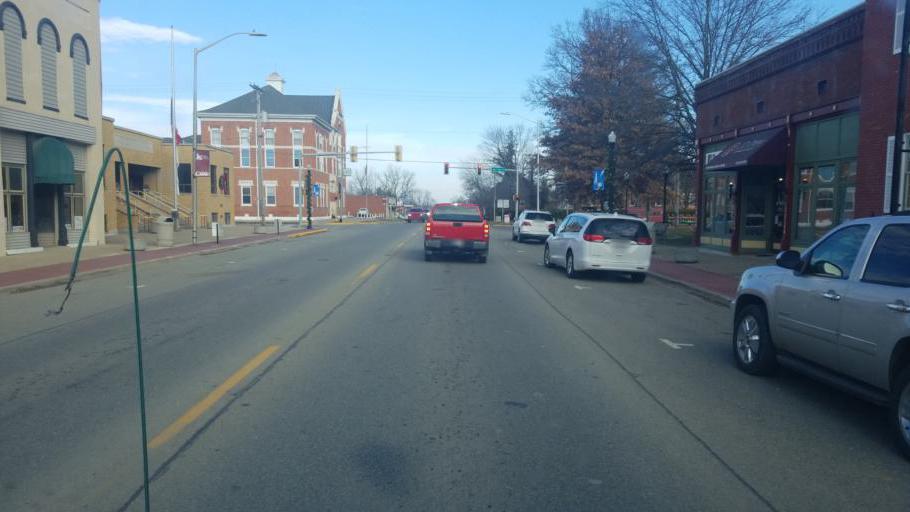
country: US
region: Illinois
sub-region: White County
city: Carmi
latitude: 38.0904
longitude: -88.1594
